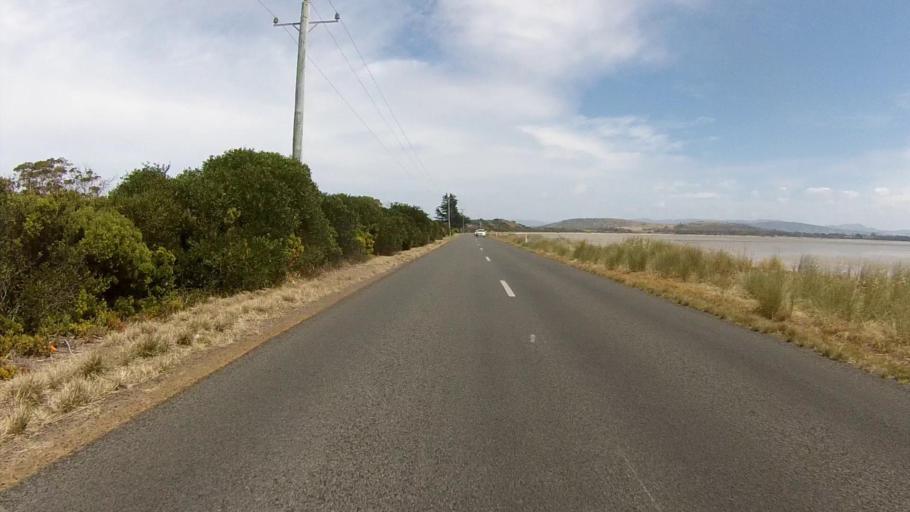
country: AU
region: Tasmania
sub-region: Clarence
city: Sandford
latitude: -43.0279
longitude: 147.4670
